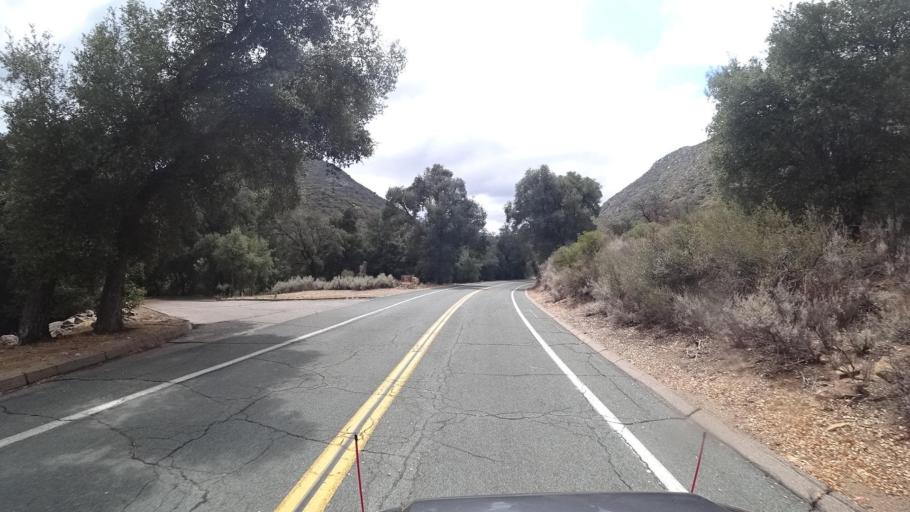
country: US
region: California
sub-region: San Diego County
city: Pine Valley
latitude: 32.7781
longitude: -116.4492
